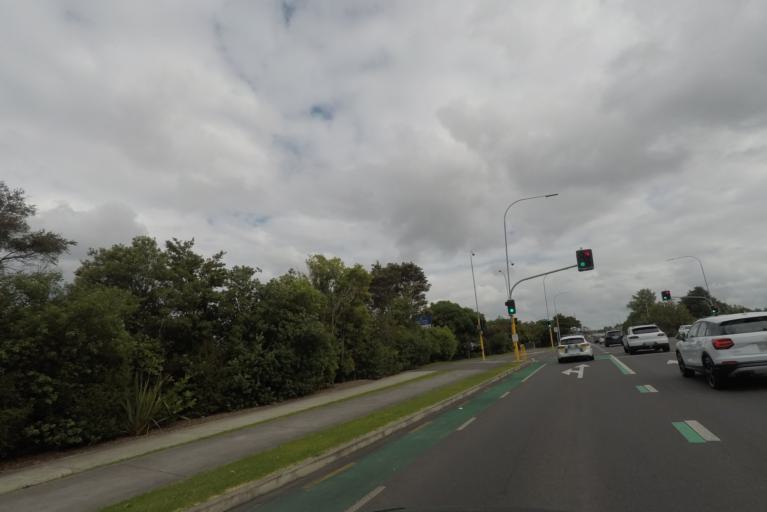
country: NZ
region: Auckland
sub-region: Auckland
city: Rothesay Bay
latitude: -36.7362
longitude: 174.6916
